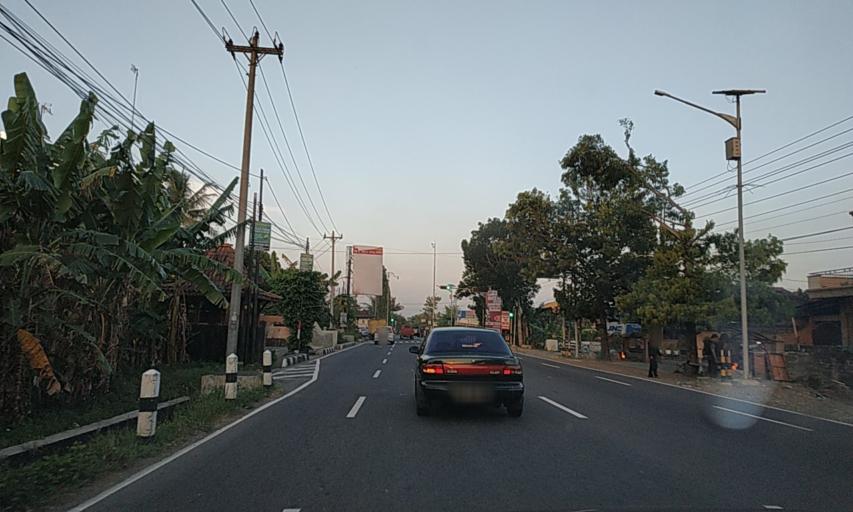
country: ID
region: Daerah Istimewa Yogyakarta
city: Srandakan
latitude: -7.8920
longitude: 110.1277
